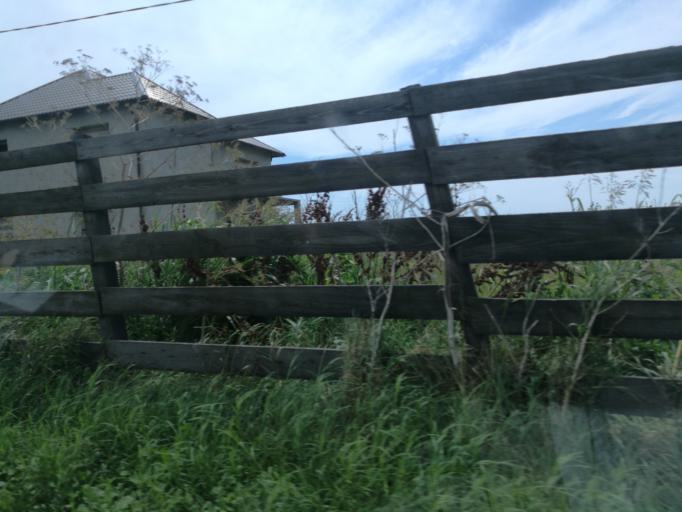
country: RO
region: Constanta
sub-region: Comuna Corbu
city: Corbu
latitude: 44.4240
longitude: 28.6674
